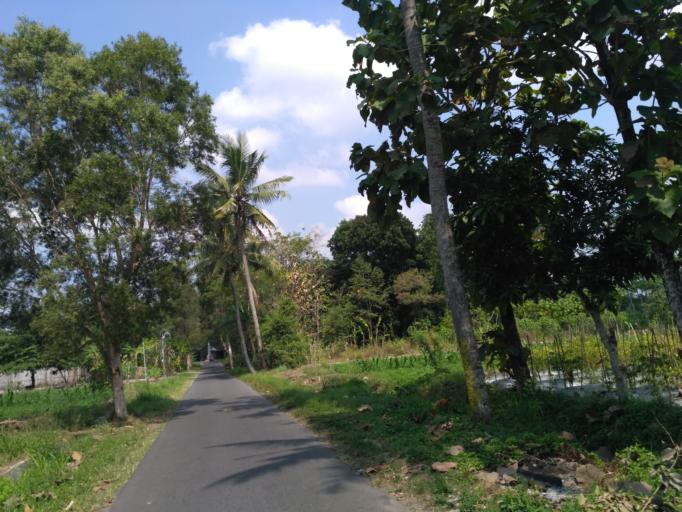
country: ID
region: Daerah Istimewa Yogyakarta
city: Depok
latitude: -7.7177
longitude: 110.4237
